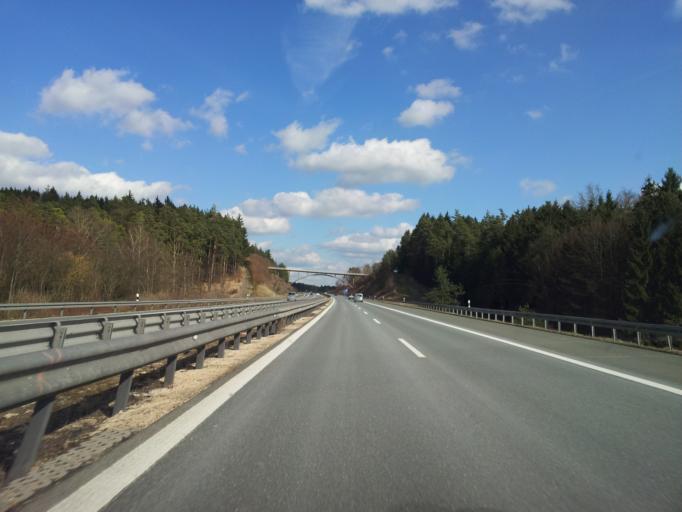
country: DE
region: Bavaria
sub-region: Upper Franconia
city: Wattendorf
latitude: 49.9909
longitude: 11.1419
